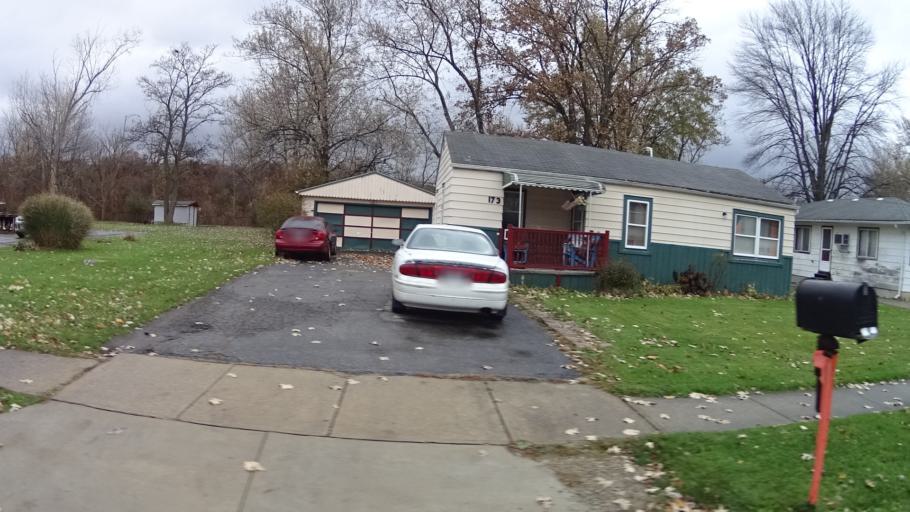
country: US
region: Ohio
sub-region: Lorain County
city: Elyria
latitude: 41.3865
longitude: -82.1257
